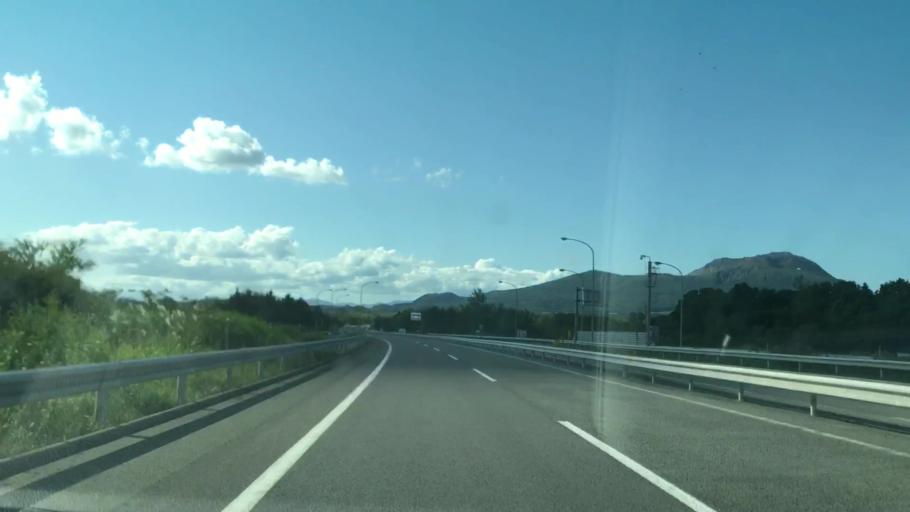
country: JP
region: Hokkaido
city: Date
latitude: 42.4848
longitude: 140.8924
